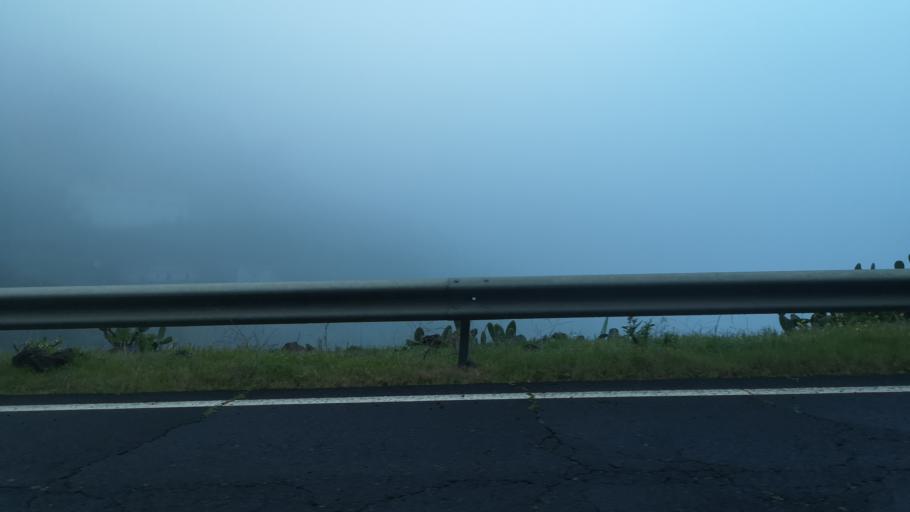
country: ES
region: Canary Islands
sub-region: Provincia de Santa Cruz de Tenerife
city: Alajero
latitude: 28.0936
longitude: -17.2035
